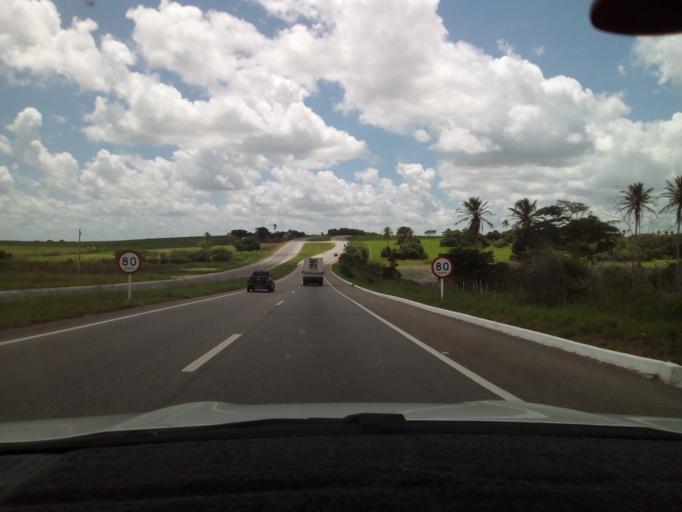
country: BR
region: Paraiba
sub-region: Pilar
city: Pilar
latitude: -7.1901
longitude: -35.2179
